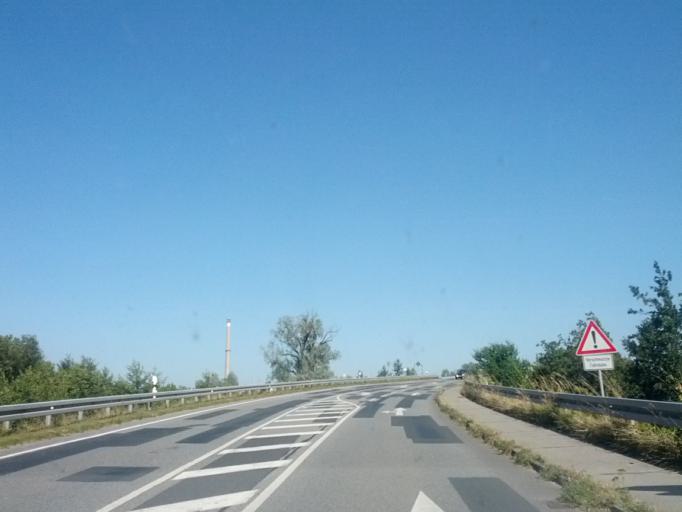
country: DE
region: Mecklenburg-Vorpommern
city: Sagard
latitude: 54.4859
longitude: 13.5770
